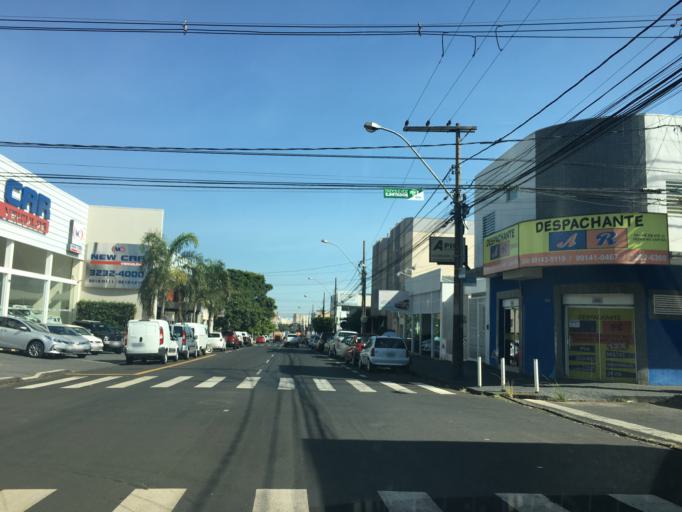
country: BR
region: Minas Gerais
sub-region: Uberlandia
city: Uberlandia
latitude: -18.8937
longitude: -48.2614
